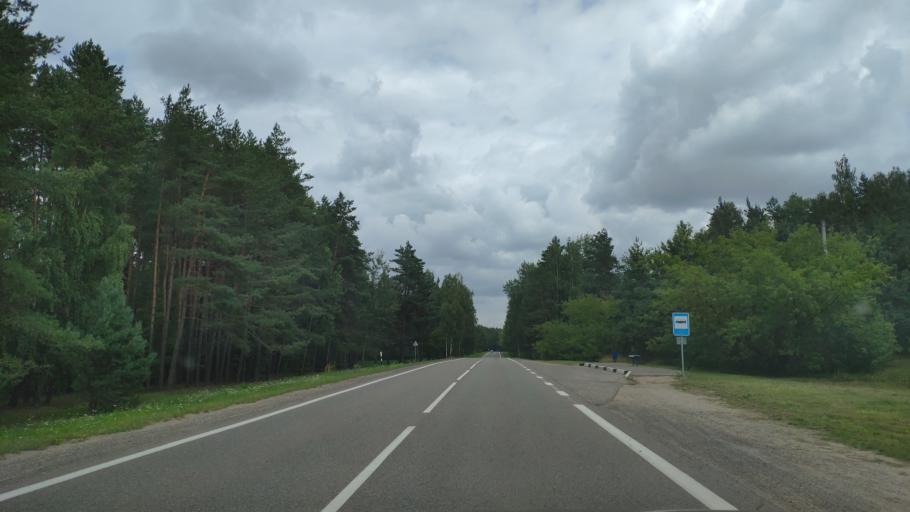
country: BY
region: Minsk
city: Zhdanovichy
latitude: 53.9725
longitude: 27.4355
